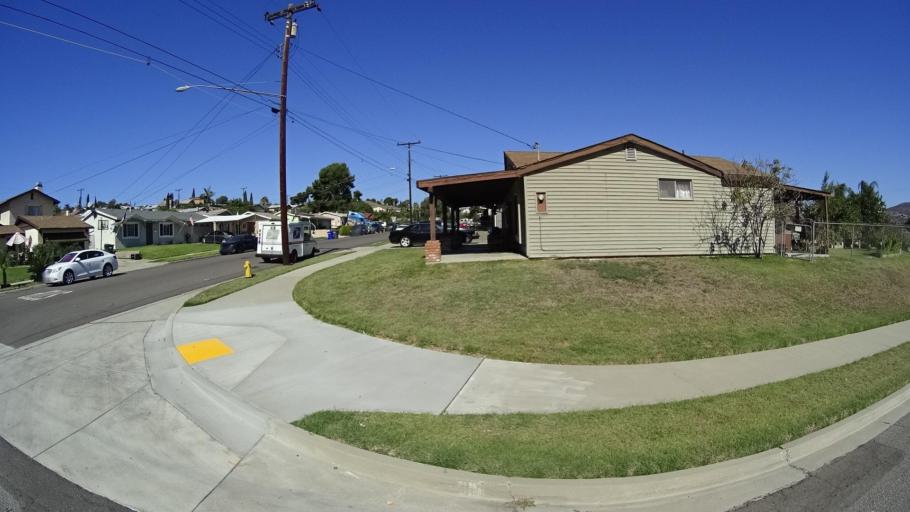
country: US
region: California
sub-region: San Diego County
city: La Presa
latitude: 32.7017
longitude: -117.0186
